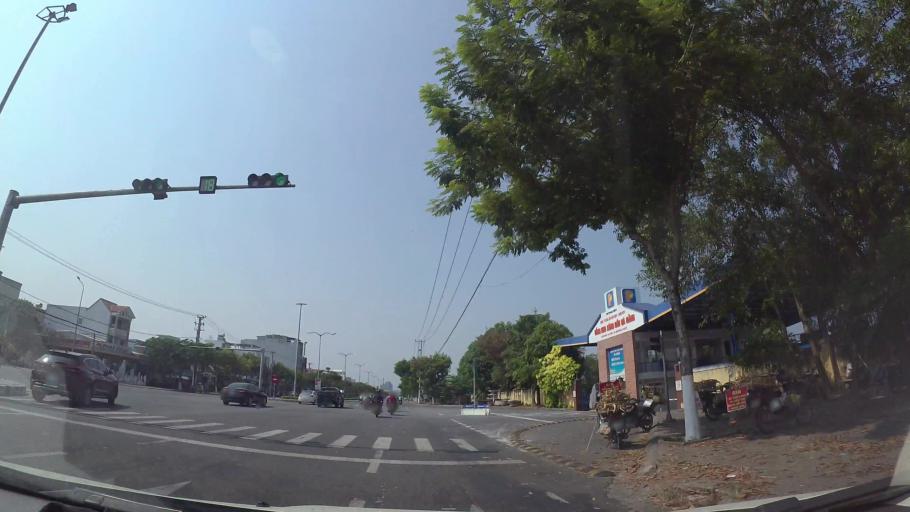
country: VN
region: Da Nang
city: Ngu Hanh Son
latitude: 16.0317
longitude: 108.2466
